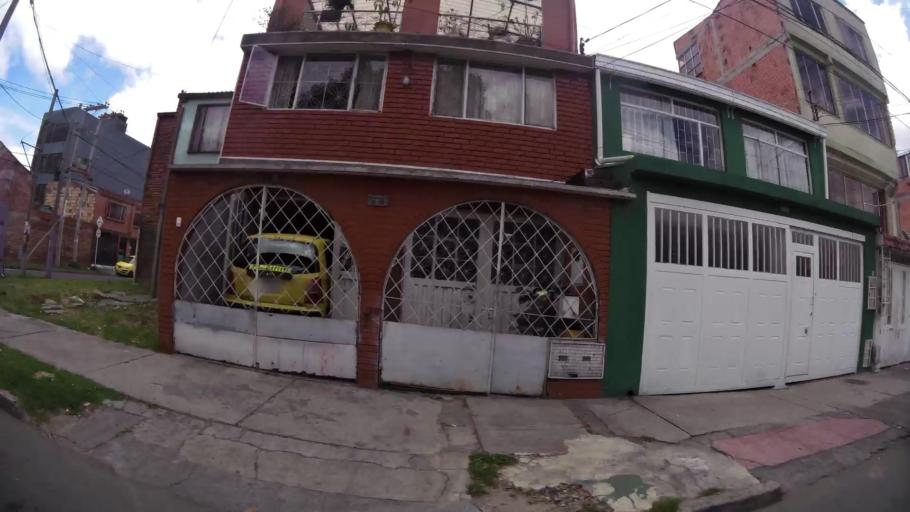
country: CO
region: Bogota D.C.
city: Bogota
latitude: 4.6090
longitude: -74.1184
